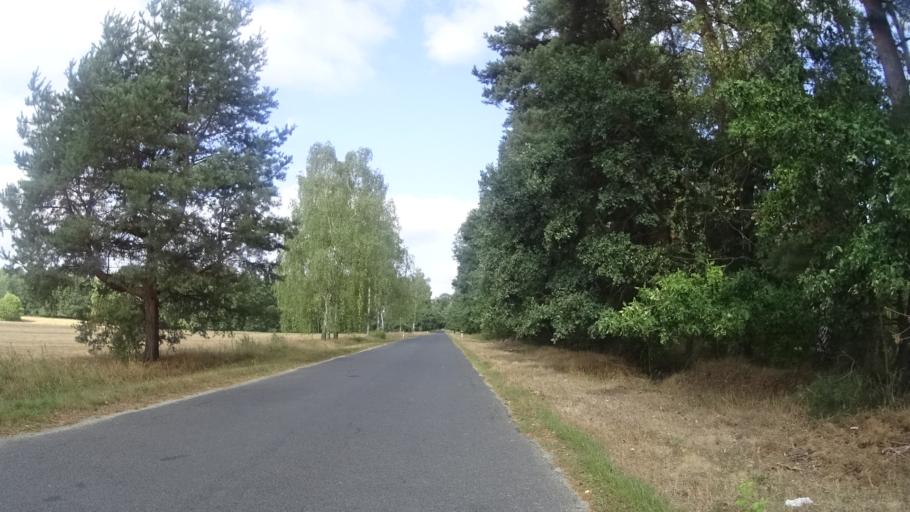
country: PL
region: Lubusz
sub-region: Powiat zarski
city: Przewoz
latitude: 51.4906
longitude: 14.8779
